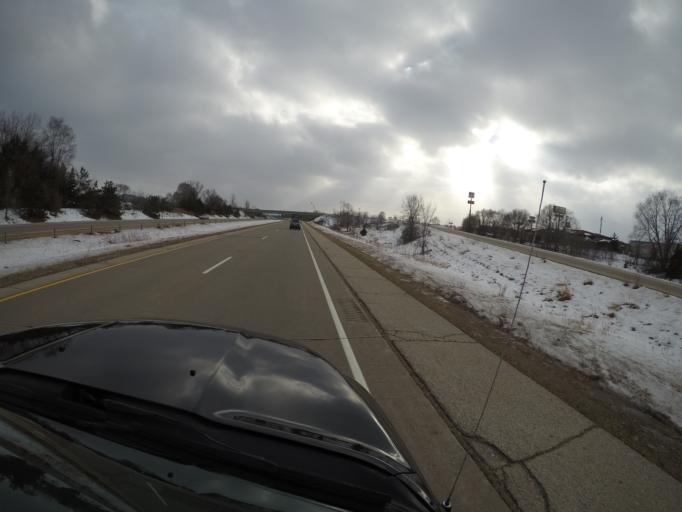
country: US
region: Wisconsin
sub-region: La Crosse County
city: Holmen
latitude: 43.9258
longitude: -91.2422
